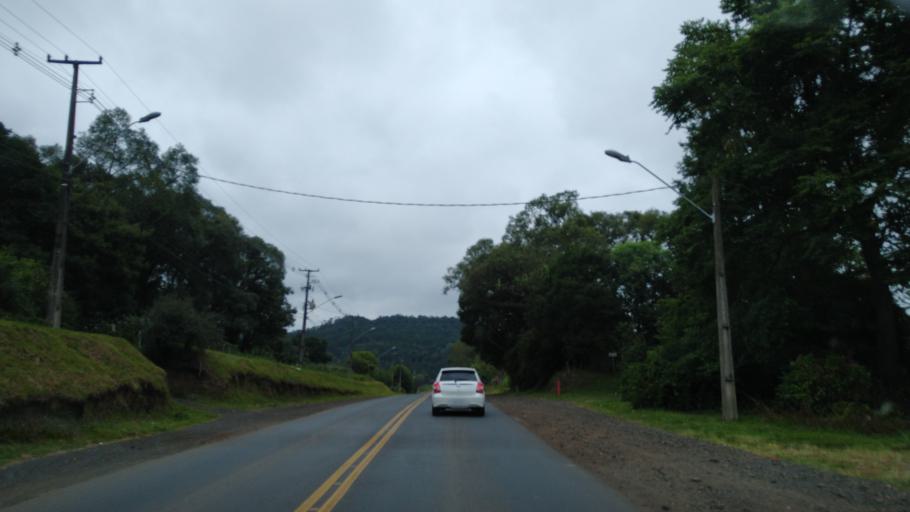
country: BR
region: Parana
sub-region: Uniao Da Vitoria
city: Uniao da Vitoria
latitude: -26.2380
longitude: -51.1248
